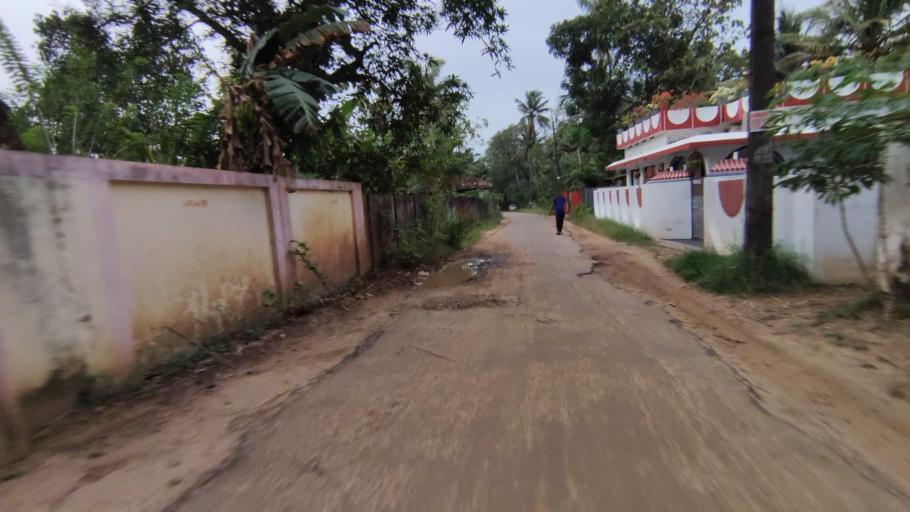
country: IN
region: Kerala
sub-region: Alappuzha
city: Shertallai
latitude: 9.6607
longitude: 76.3637
